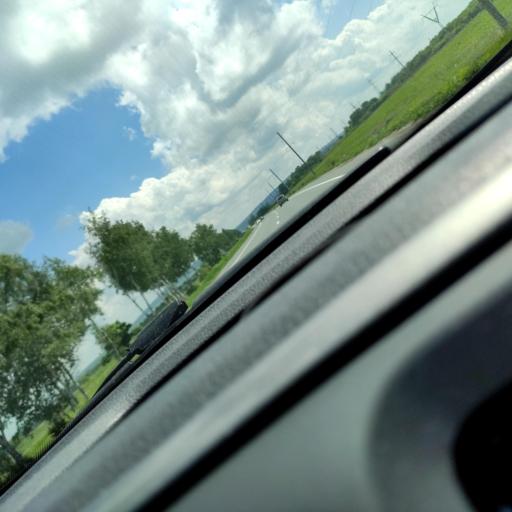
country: RU
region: Samara
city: Kurumoch
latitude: 53.4911
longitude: 49.9755
